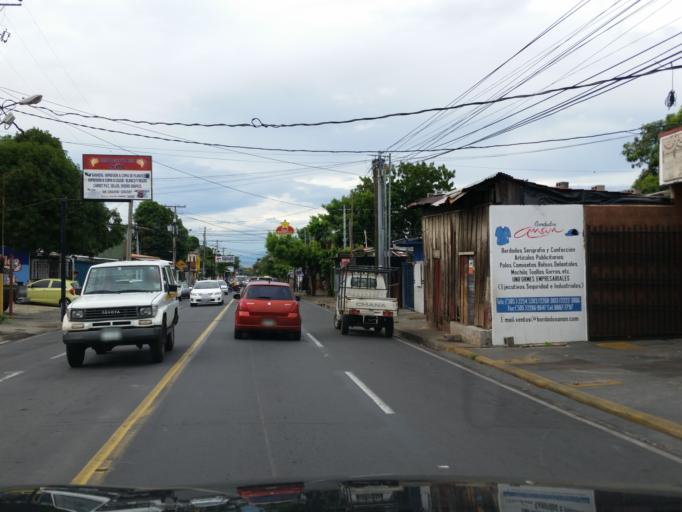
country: NI
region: Managua
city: Managua
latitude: 12.1426
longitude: -86.2827
